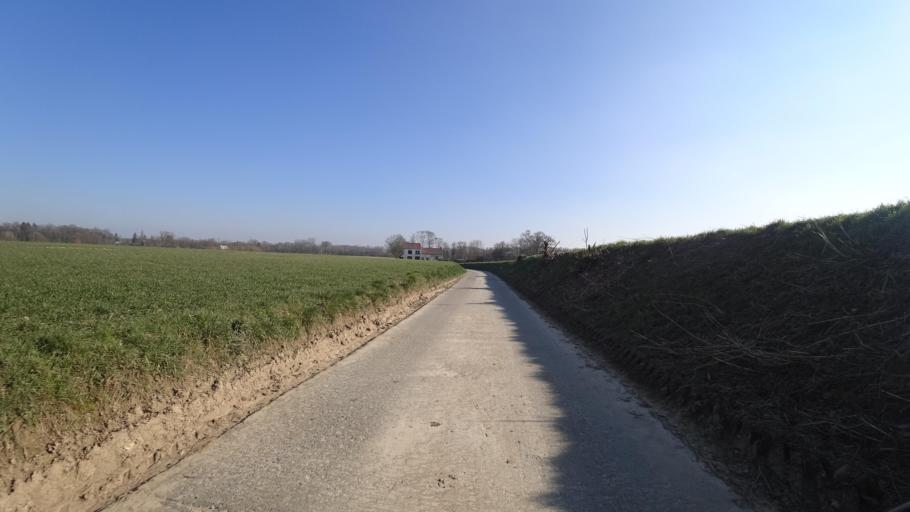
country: BE
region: Wallonia
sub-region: Province du Brabant Wallon
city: Chastre
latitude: 50.5746
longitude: 4.6394
